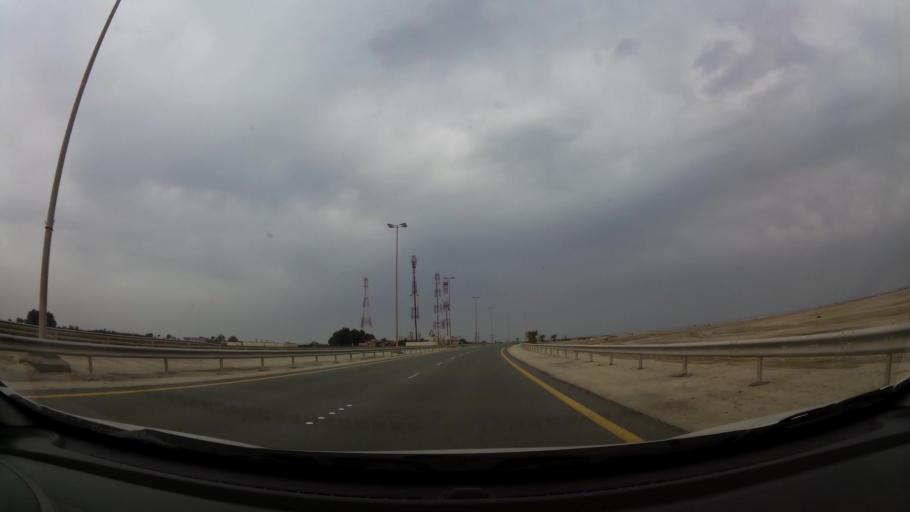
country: BH
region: Central Governorate
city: Dar Kulayb
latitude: 25.9942
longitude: 50.4710
